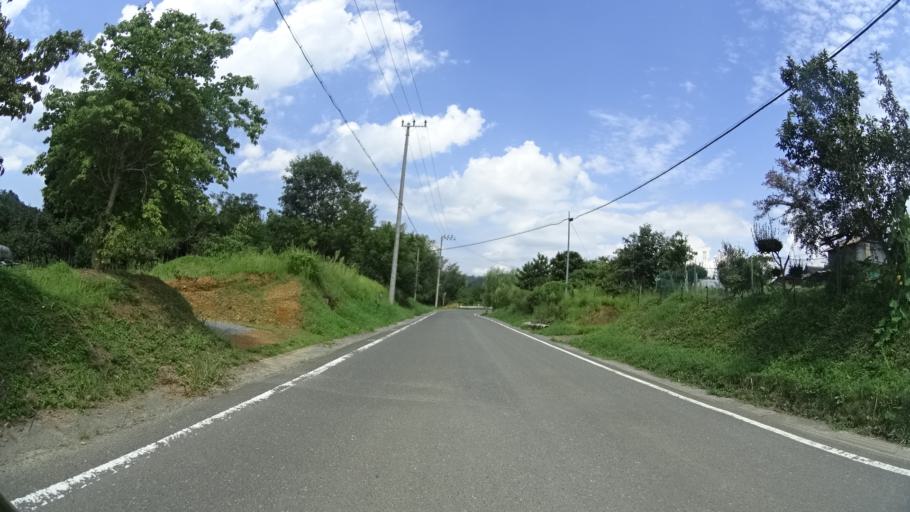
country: JP
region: Kyoto
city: Maizuru
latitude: 35.3637
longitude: 135.3202
